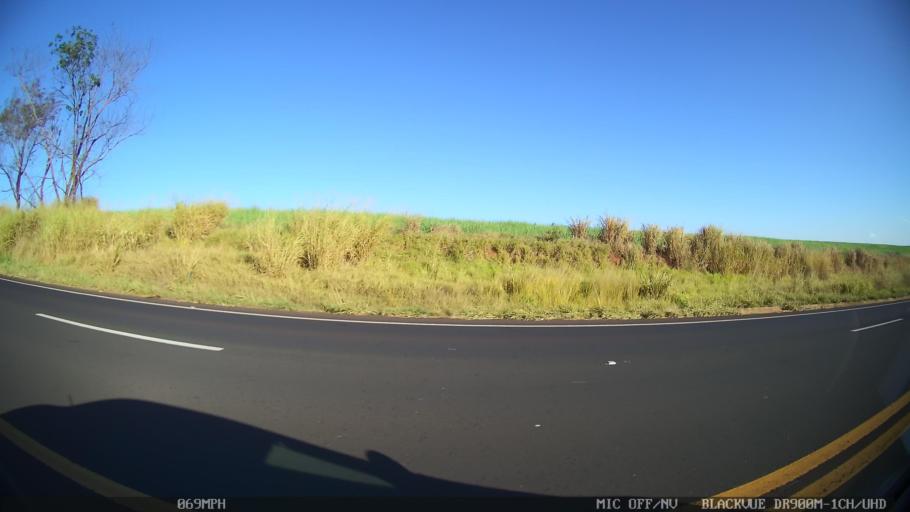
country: BR
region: Sao Paulo
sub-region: Guapiacu
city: Guapiacu
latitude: -20.7400
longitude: -49.0925
